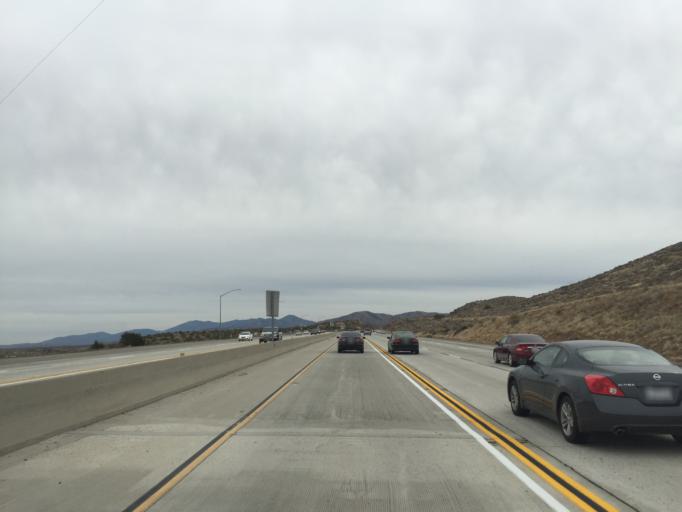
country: US
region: California
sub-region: Los Angeles County
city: Palmdale
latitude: 34.5426
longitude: -118.1254
